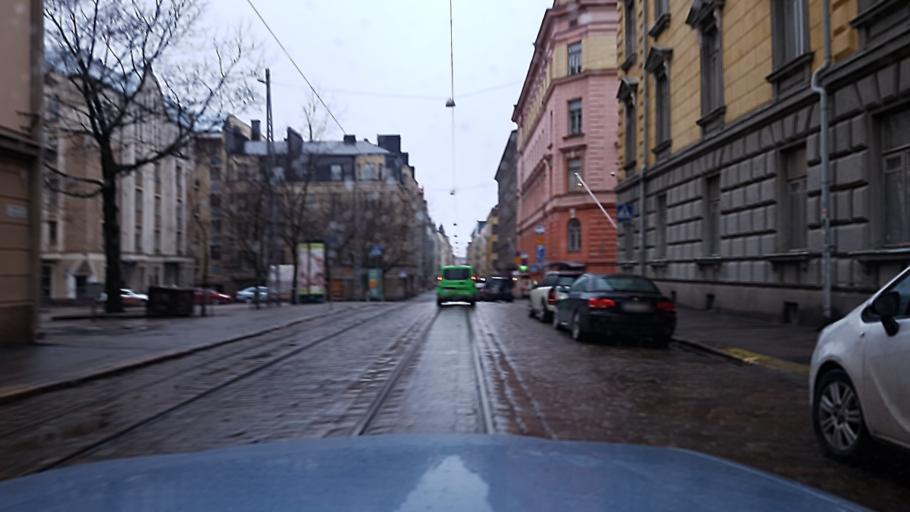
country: FI
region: Uusimaa
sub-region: Helsinki
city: Helsinki
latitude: 60.1616
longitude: 24.9409
